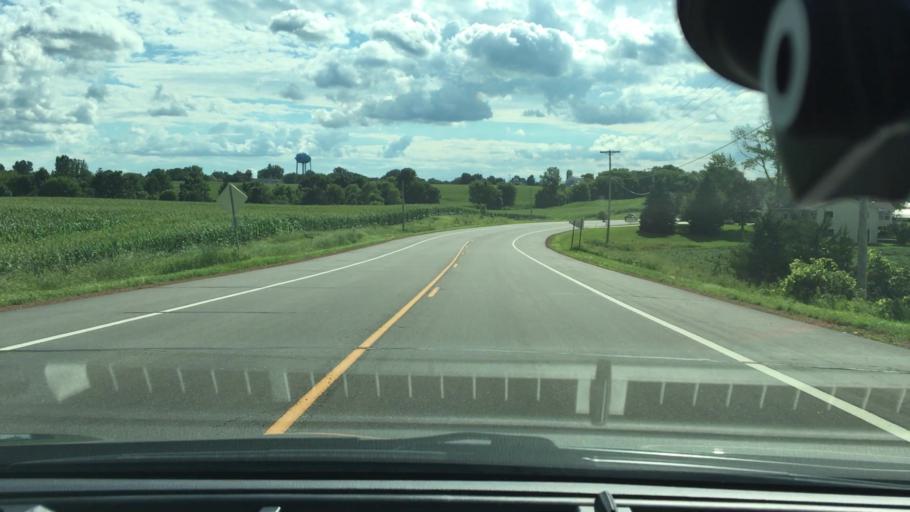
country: US
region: Minnesota
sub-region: Hennepin County
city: Saint Bonifacius
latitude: 44.9173
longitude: -93.7390
